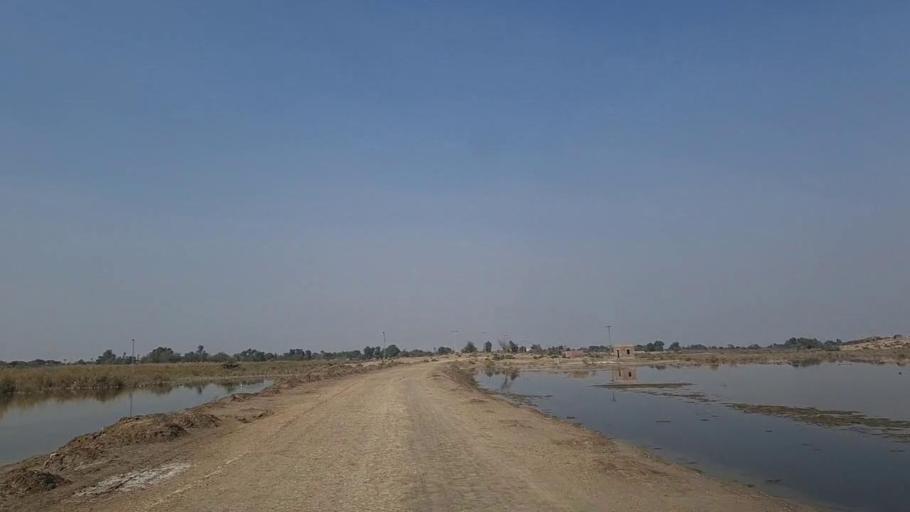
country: PK
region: Sindh
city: Daur
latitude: 26.5083
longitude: 68.4795
